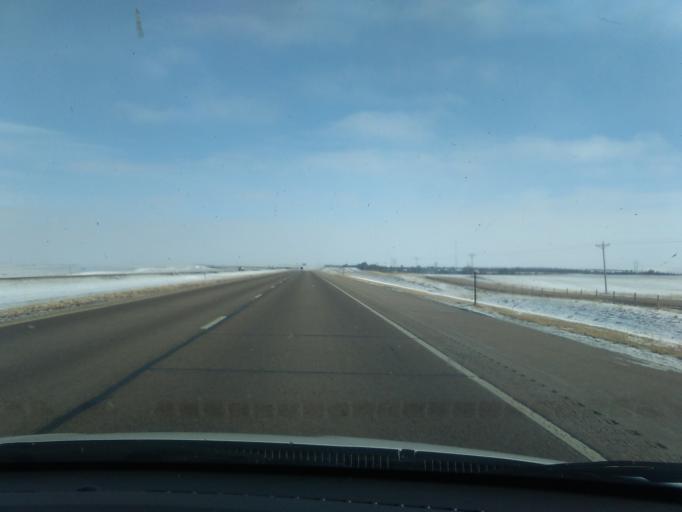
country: US
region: Nebraska
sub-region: Kimball County
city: Kimball
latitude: 41.1918
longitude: -103.7851
